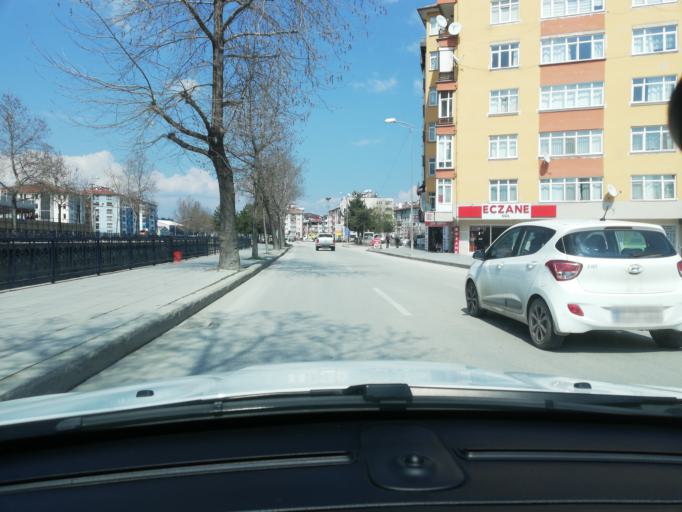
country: TR
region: Kastamonu
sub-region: Cide
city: Kastamonu
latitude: 41.3904
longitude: 33.7815
